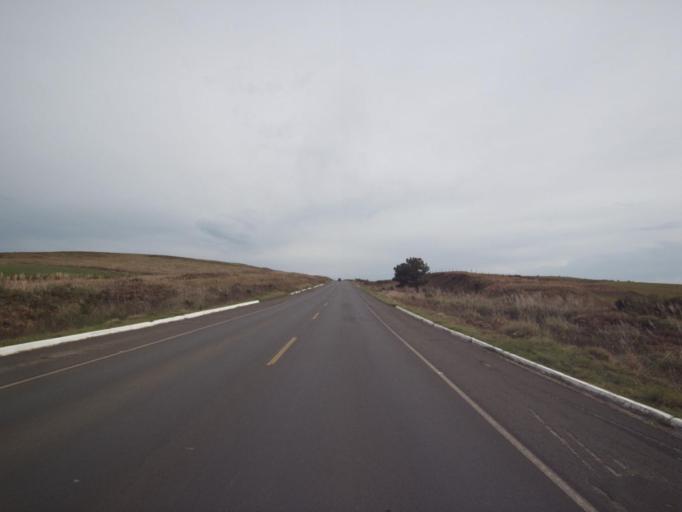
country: BR
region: Parana
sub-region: Palmas
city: Palmas
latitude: -26.7271
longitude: -51.6361
